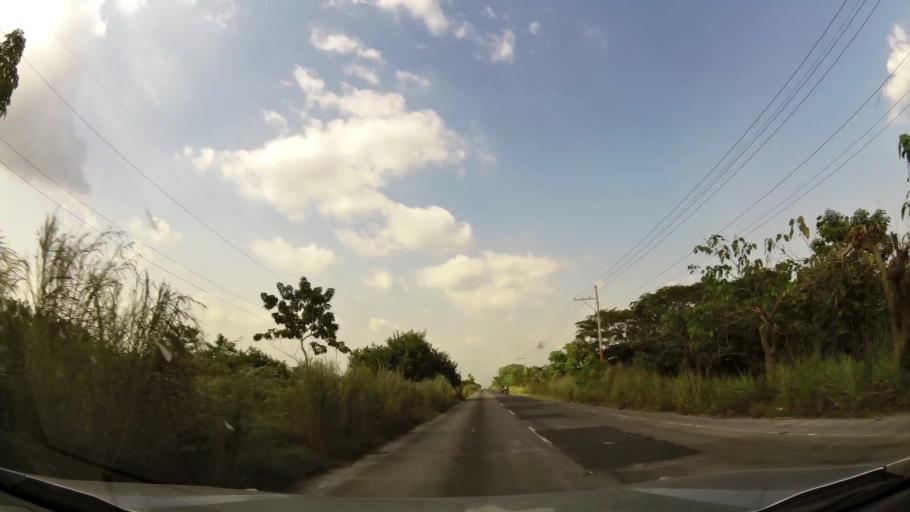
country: GT
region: Escuintla
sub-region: Municipio de Masagua
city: Masagua
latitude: 14.1114
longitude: -90.7810
